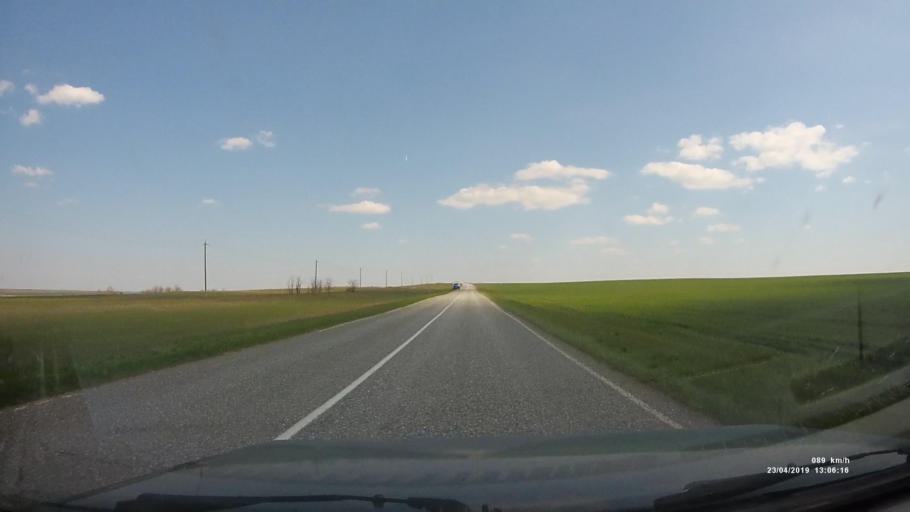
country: RU
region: Kalmykiya
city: Yashalta
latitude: 46.5918
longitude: 42.7381
